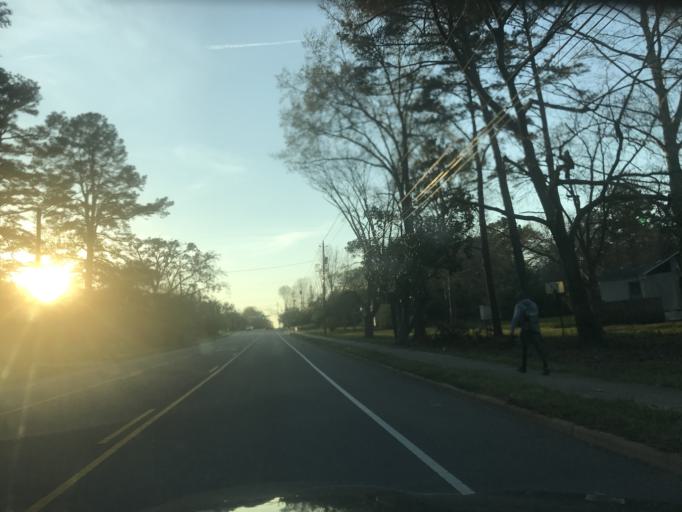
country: US
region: North Carolina
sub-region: Wake County
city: Raleigh
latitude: 35.7740
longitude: -78.6033
